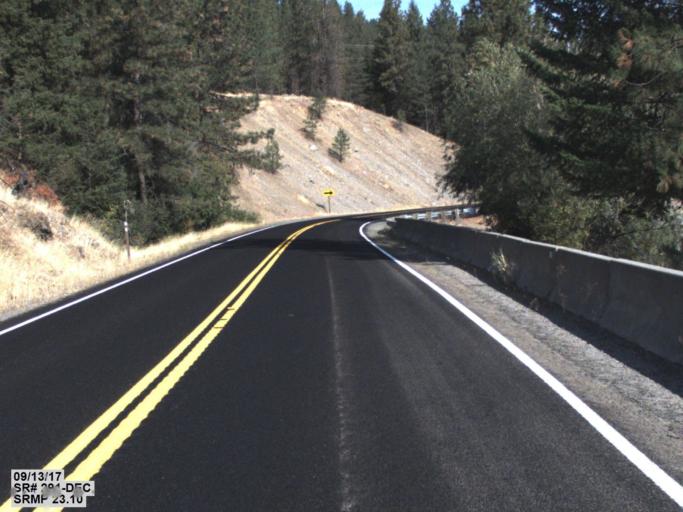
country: US
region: Washington
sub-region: Spokane County
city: Deer Park
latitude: 47.8833
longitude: -117.6977
